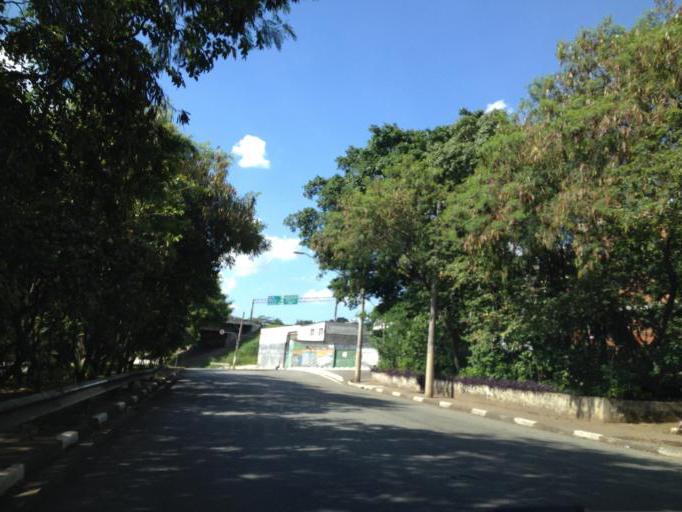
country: BR
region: Sao Paulo
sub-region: Guarulhos
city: Guarulhos
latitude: -23.5089
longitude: -46.5710
